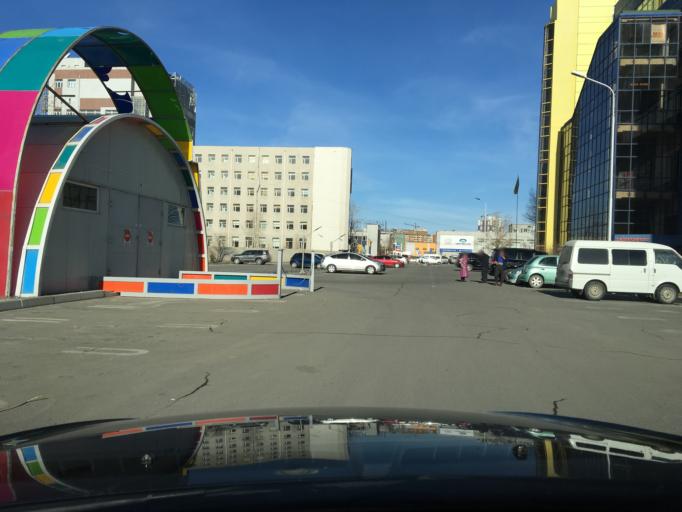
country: MN
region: Ulaanbaatar
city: Ulaanbaatar
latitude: 47.8959
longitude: 106.8890
